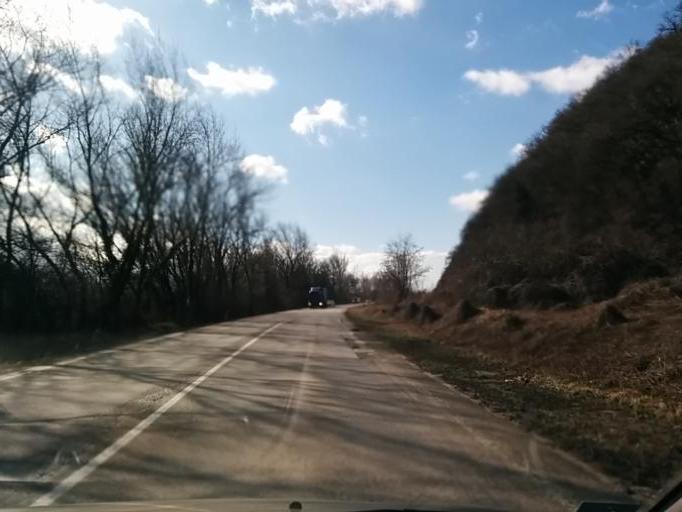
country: SK
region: Trenciansky
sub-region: Okres Nove Mesto nad Vahom
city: Nove Mesto nad Vahom
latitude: 48.7844
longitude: 17.8646
